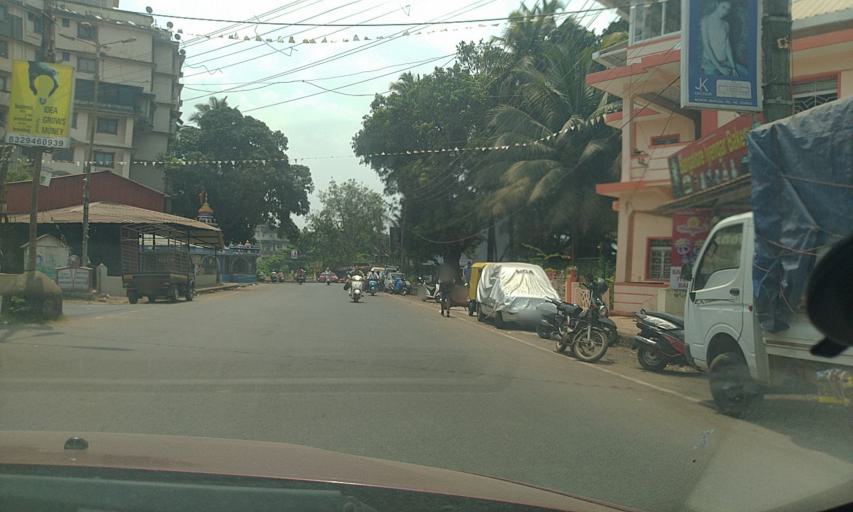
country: IN
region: Goa
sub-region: North Goa
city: Mapuca
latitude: 15.5922
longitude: 73.8069
